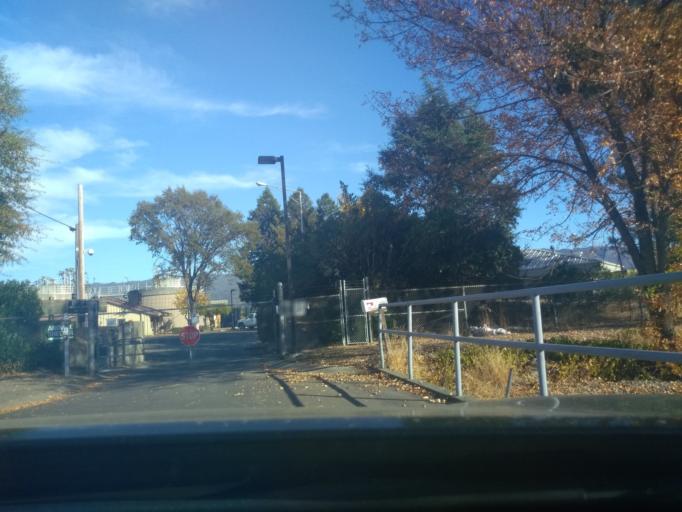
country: US
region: California
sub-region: Mendocino County
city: Talmage
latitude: 39.1124
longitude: -123.1925
